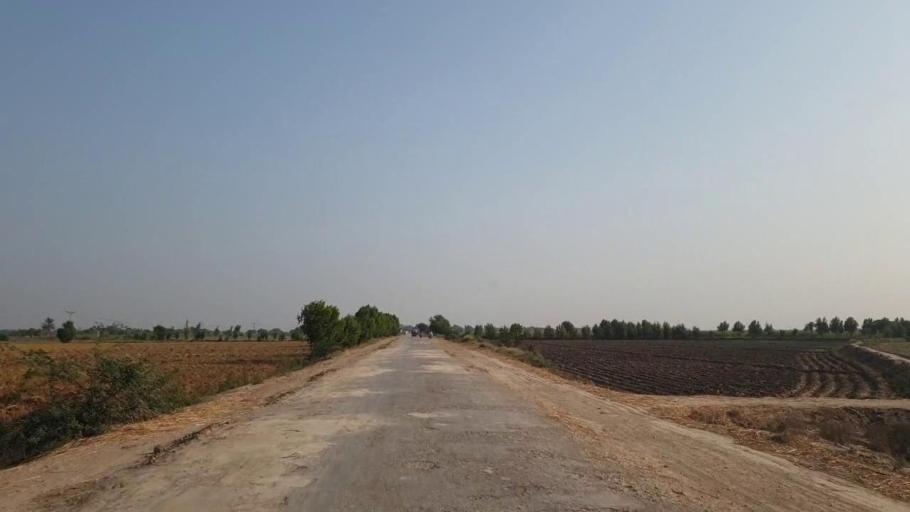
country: PK
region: Sindh
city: Bulri
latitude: 24.9933
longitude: 68.3846
